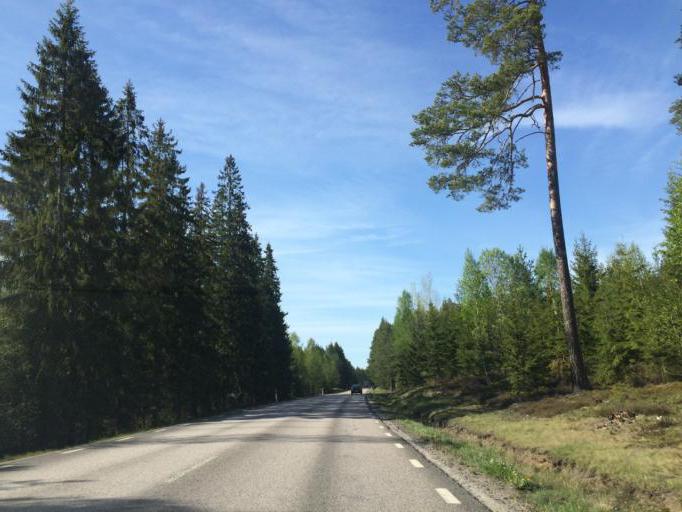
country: SE
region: Soedermanland
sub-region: Katrineholms Kommun
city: Katrineholm
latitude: 59.1015
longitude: 16.1840
